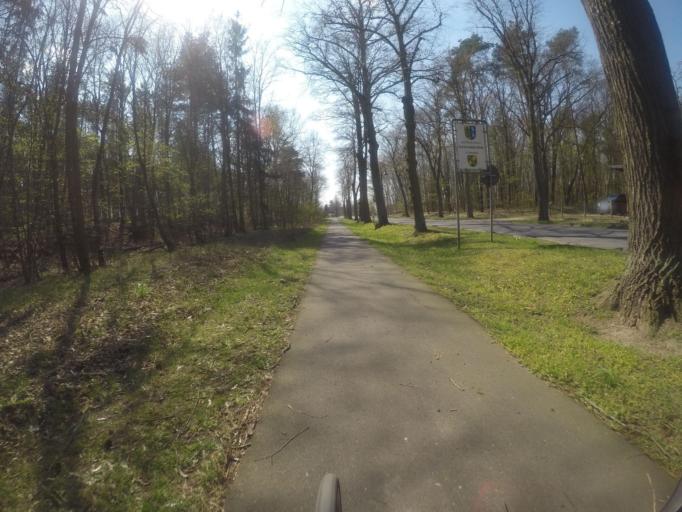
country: DE
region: Brandenburg
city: Brieselang
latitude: 52.6493
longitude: 13.0052
